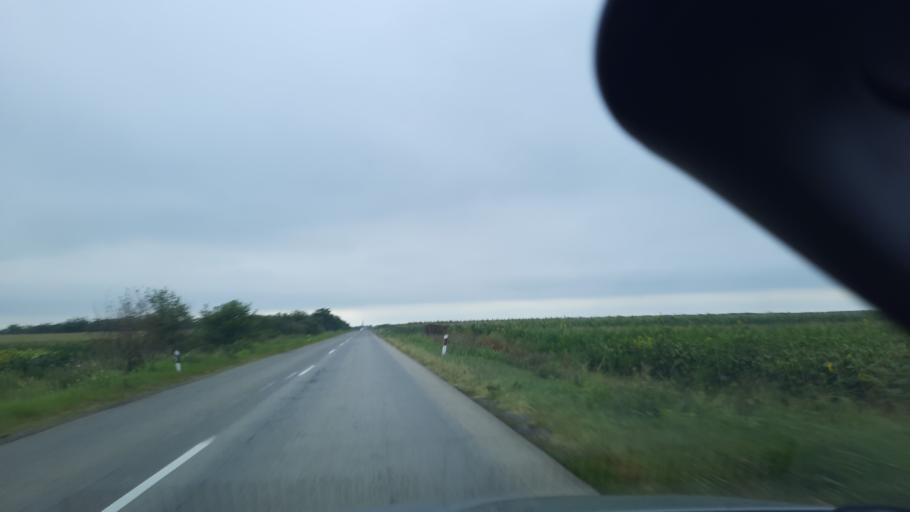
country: RS
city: Farkazdin
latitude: 45.1988
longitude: 20.4423
